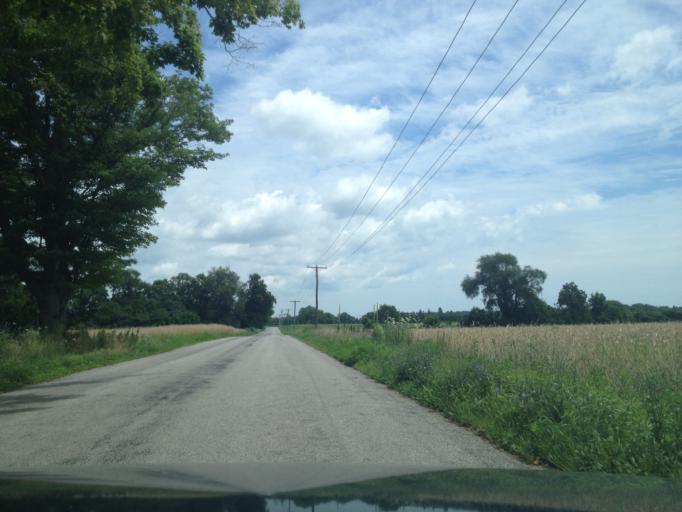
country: CA
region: Ontario
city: Norfolk County
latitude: 42.7819
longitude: -80.2915
